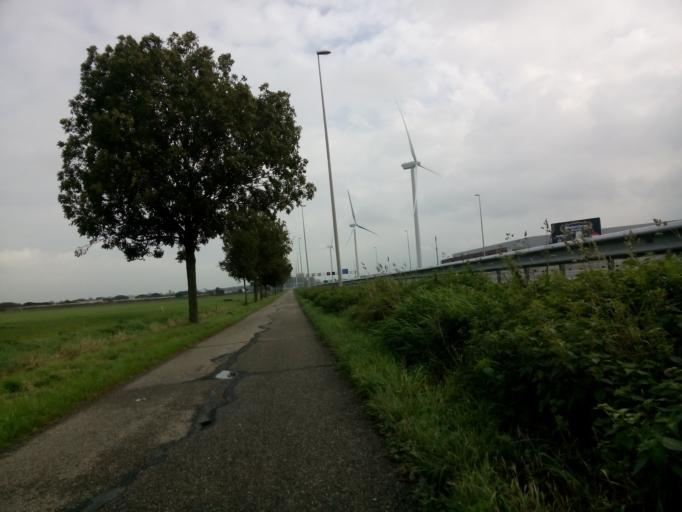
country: NL
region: South Holland
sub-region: Gemeente Waddinxveen
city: Waddinxveen
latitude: 52.0200
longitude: 4.6254
